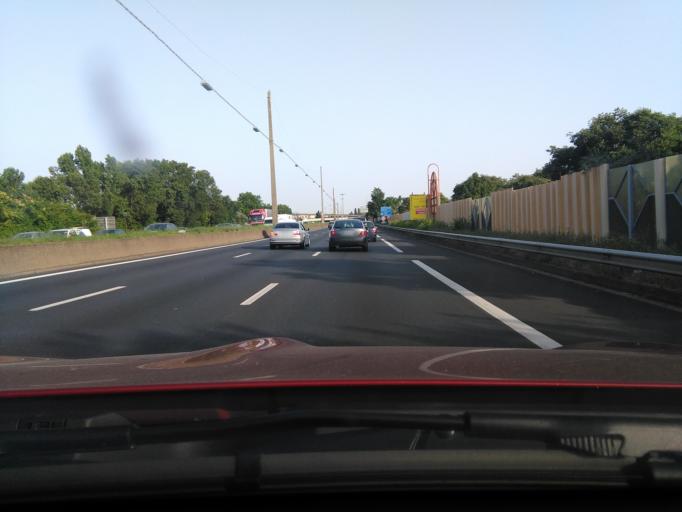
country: FR
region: Rhone-Alpes
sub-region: Departement du Rhone
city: Villeurbanne
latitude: 45.7715
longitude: 4.9015
